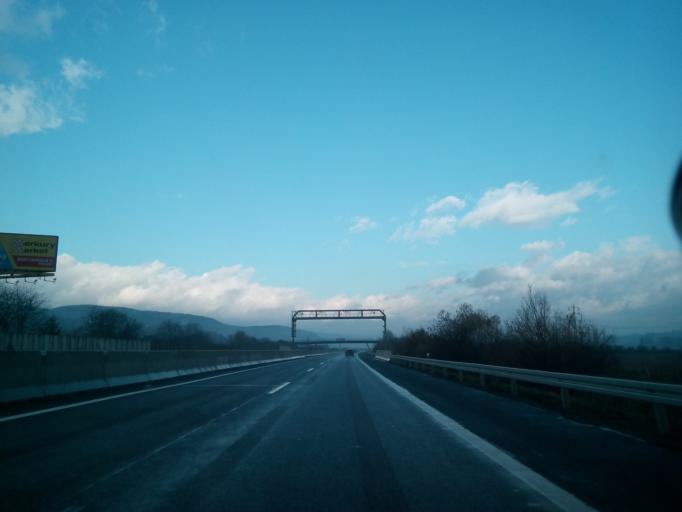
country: SK
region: Presovsky
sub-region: Okres Presov
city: Presov
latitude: 48.8749
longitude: 21.2533
